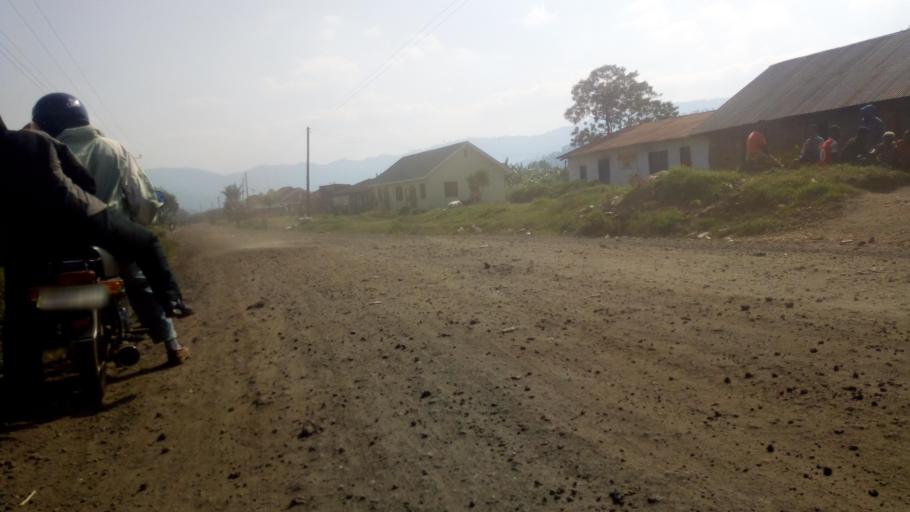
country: UG
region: Western Region
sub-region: Kisoro District
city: Kisoro
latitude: -1.2464
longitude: 29.7134
